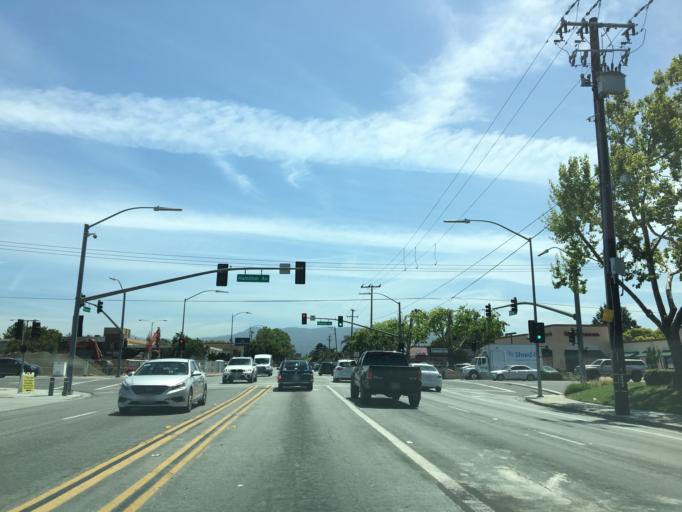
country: US
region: California
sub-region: Santa Clara County
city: Buena Vista
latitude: 37.2950
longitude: -121.9136
